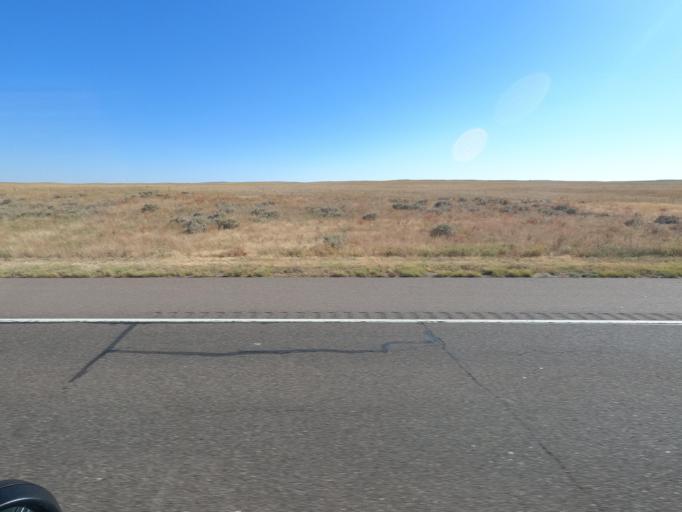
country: US
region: Nebraska
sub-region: Deuel County
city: Chappell
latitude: 40.8728
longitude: -102.6248
